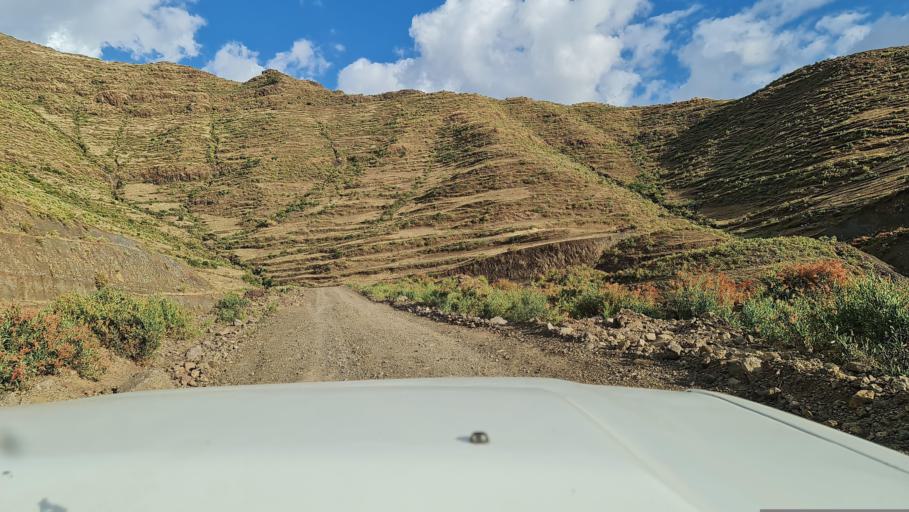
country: ET
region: Amhara
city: Debark'
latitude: 13.0495
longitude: 38.0205
